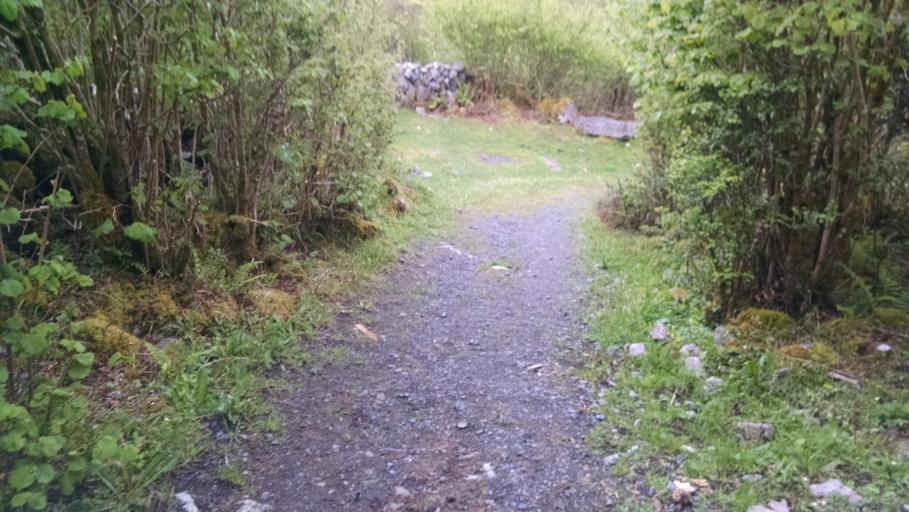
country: IE
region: Munster
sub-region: An Clar
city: Ennis
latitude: 53.0123
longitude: -9.0740
